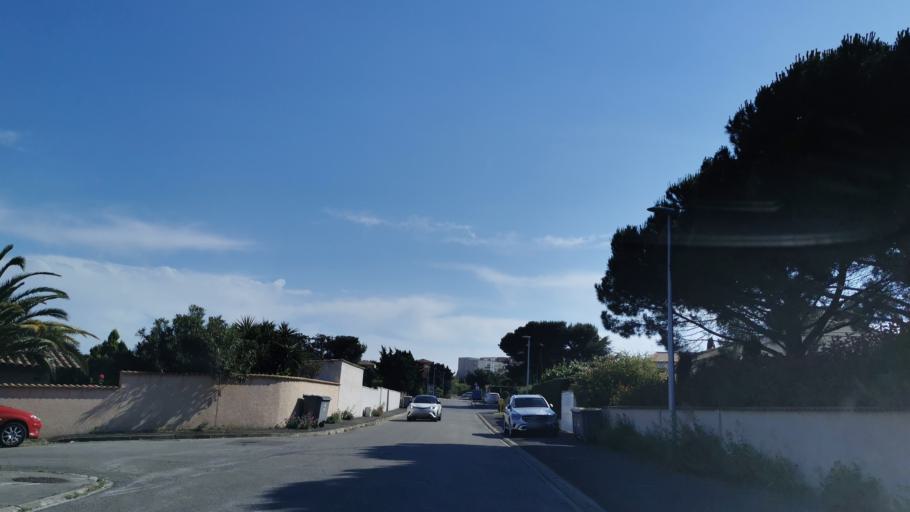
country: FR
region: Languedoc-Roussillon
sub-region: Departement de l'Aude
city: Narbonne
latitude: 43.1424
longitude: 2.9678
